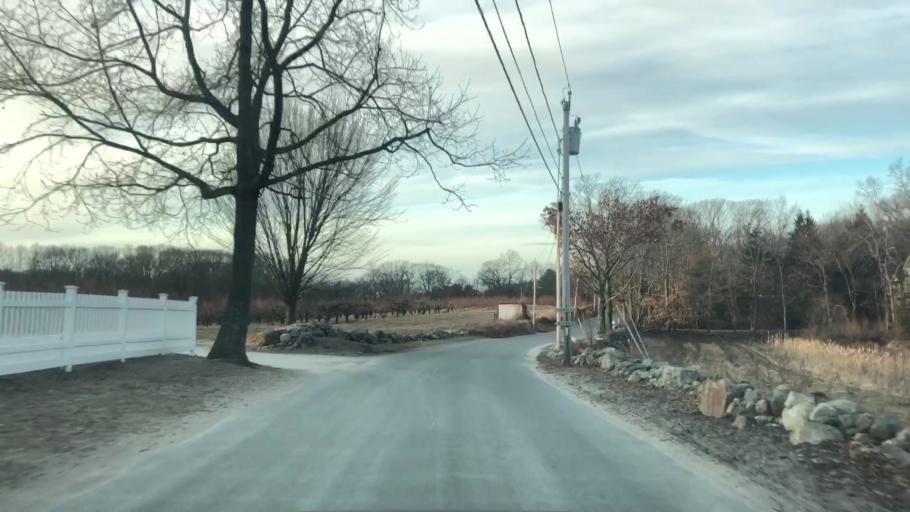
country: US
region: Massachusetts
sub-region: Essex County
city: North Andover
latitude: 42.6904
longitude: -71.0751
